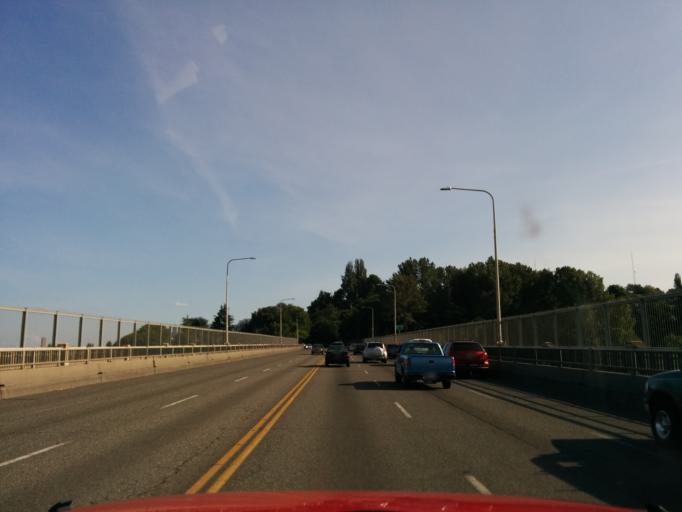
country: US
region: Washington
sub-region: King County
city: Seattle
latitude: 47.6456
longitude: -122.3473
